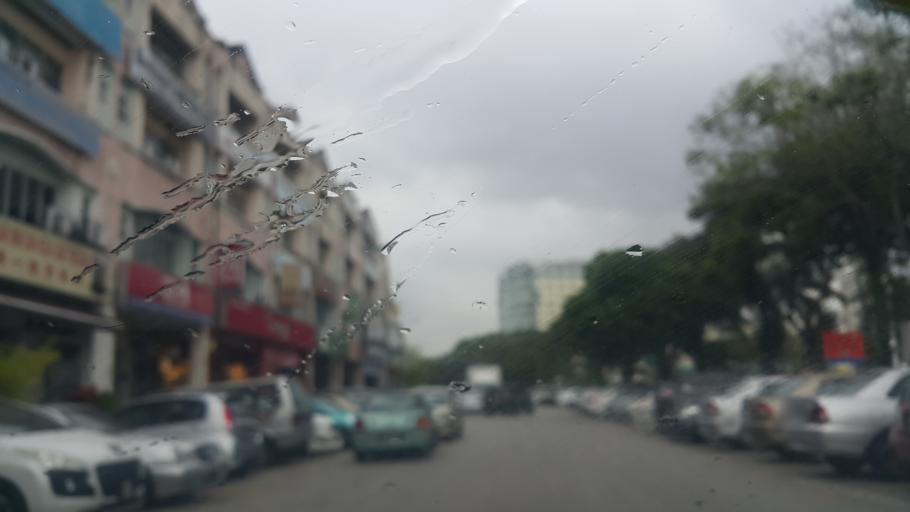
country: MY
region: Selangor
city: Klang
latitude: 3.0073
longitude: 101.4377
